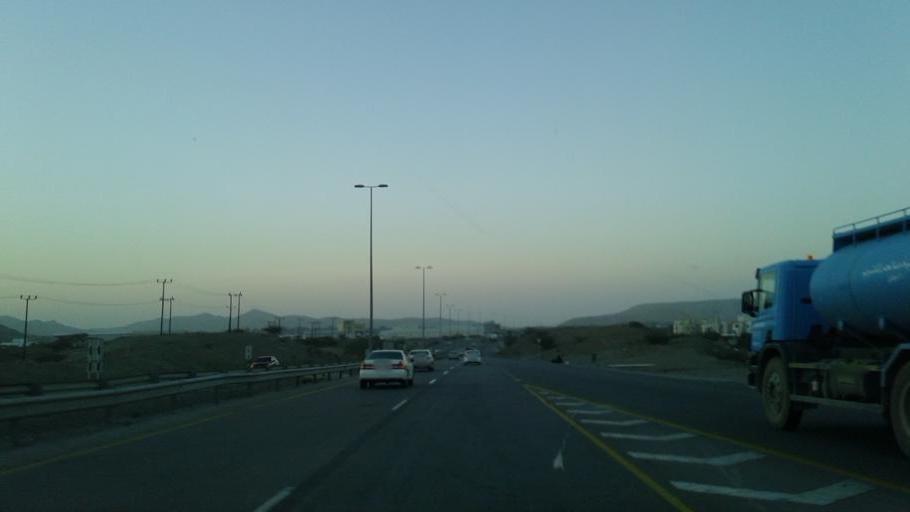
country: OM
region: Muhafazat ad Dakhiliyah
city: Bidbid
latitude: 23.4876
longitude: 58.1971
